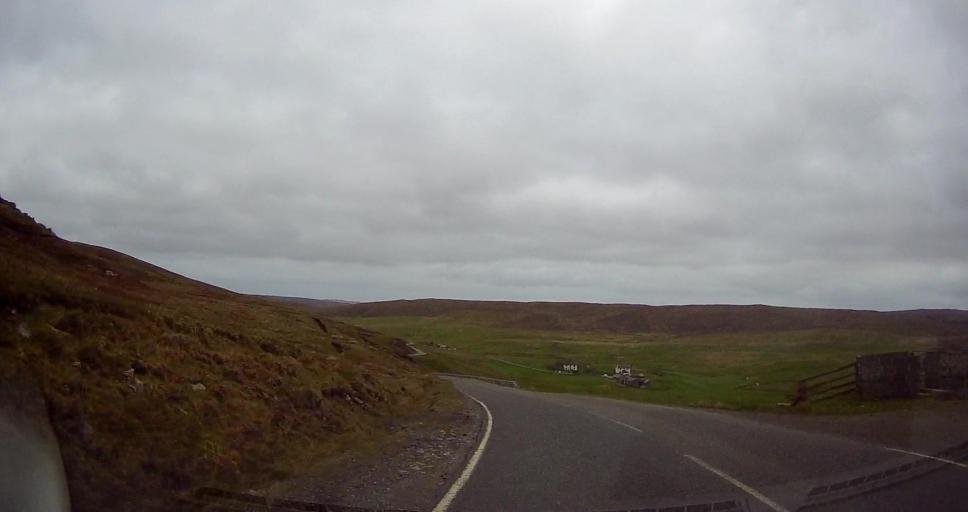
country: GB
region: Scotland
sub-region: Shetland Islands
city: Lerwick
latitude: 60.3422
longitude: -1.2903
